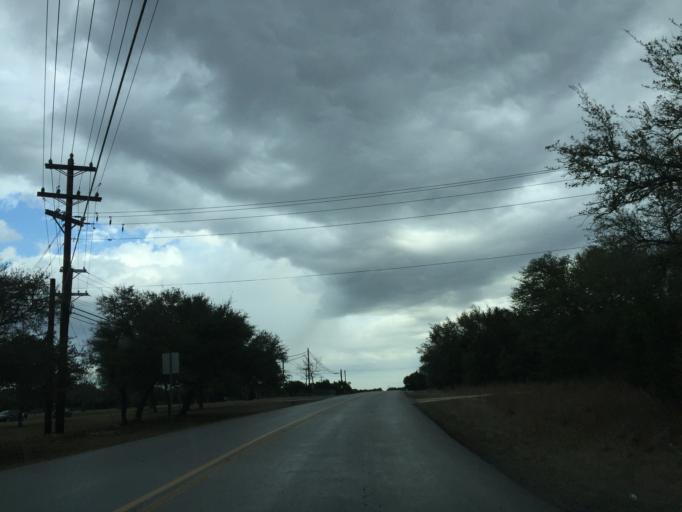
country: US
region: Texas
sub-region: Travis County
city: Jonestown
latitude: 30.5739
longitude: -97.9492
